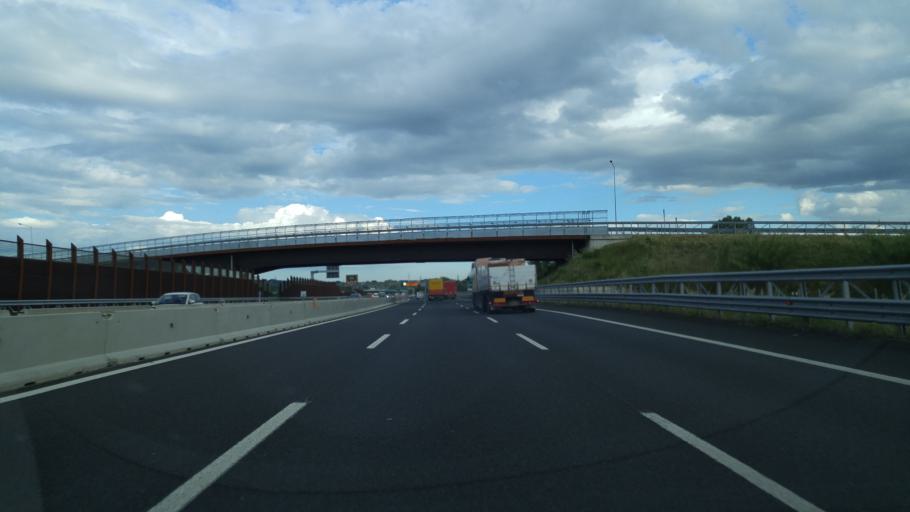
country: IT
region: Emilia-Romagna
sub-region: Provincia di Rimini
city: Coriano
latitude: 43.9921
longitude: 12.6239
